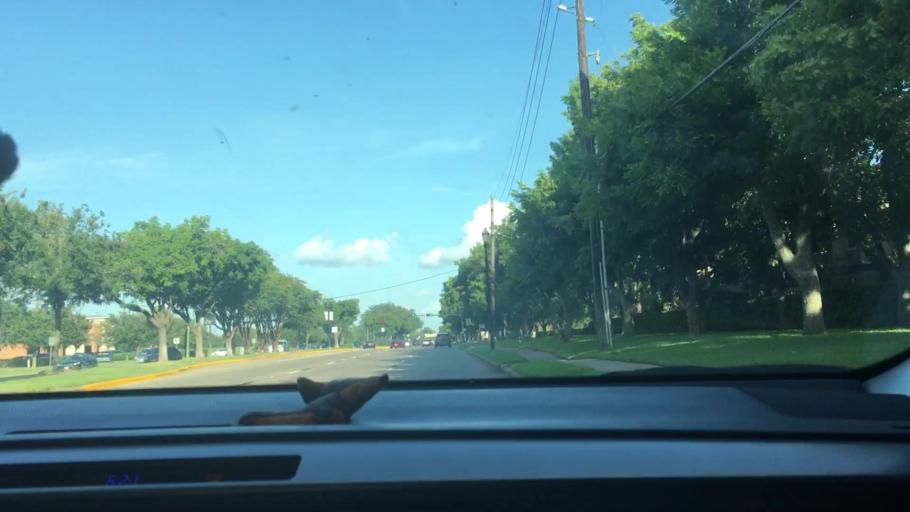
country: US
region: Texas
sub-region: Fort Bend County
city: Sugar Land
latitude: 29.6011
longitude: -95.6304
